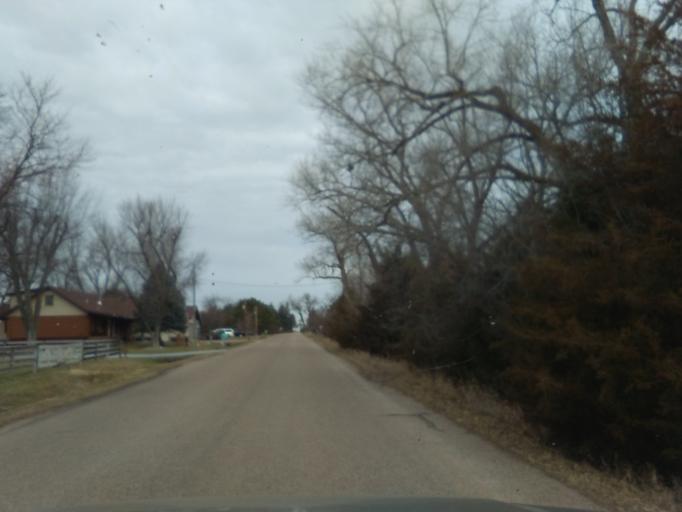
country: US
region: Nebraska
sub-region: Hall County
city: Grand Island
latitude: 40.7746
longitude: -98.4119
